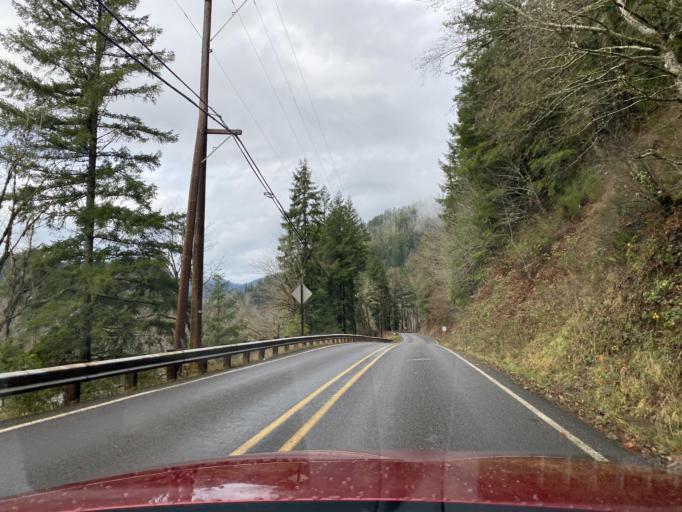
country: US
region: Oregon
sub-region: Lane County
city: Oakridge
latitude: 43.7552
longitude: -122.5259
